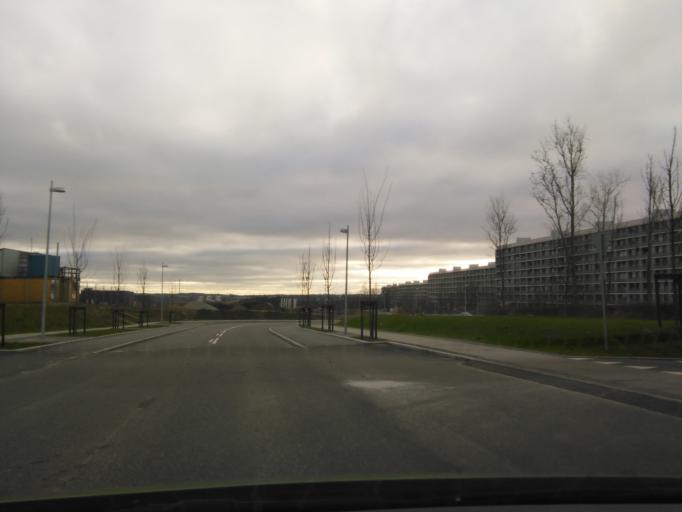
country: DK
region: Central Jutland
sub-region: Arhus Kommune
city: Stavtrup
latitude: 56.1618
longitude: 10.1410
